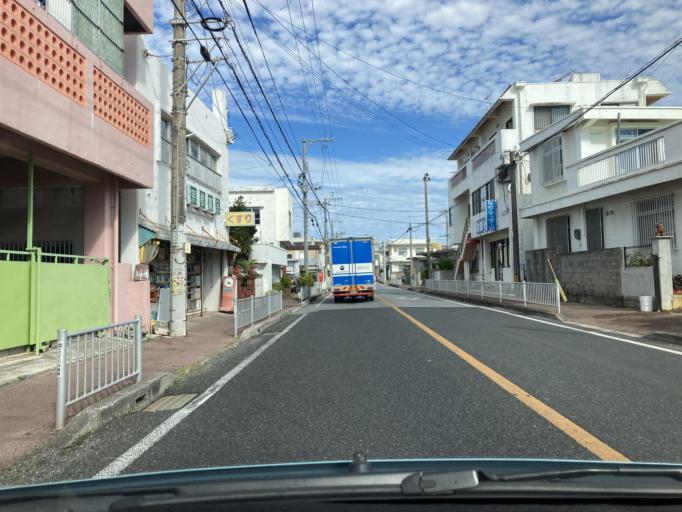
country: JP
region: Okinawa
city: Ishikawa
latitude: 26.4096
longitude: 127.7322
